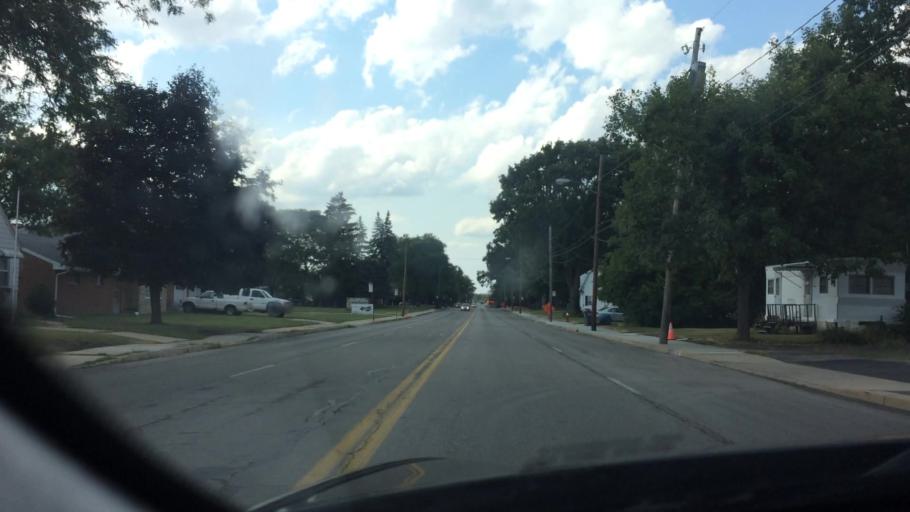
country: US
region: Ohio
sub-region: Wood County
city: Perrysburg
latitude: 41.5905
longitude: -83.6160
